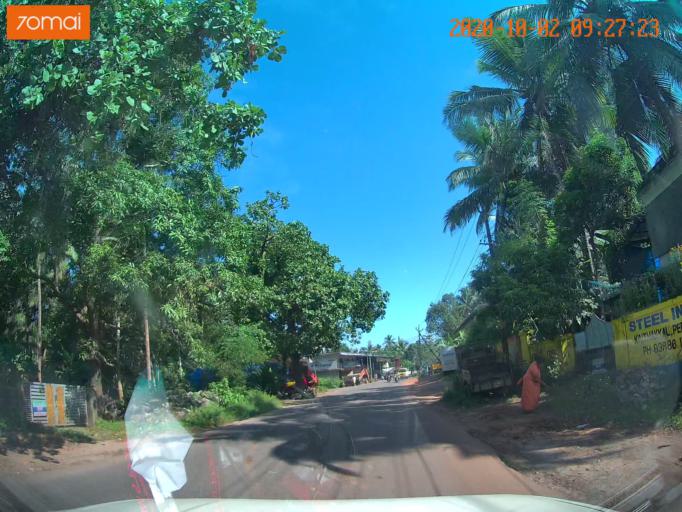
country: IN
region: Kerala
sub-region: Kozhikode
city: Naduvannur
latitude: 11.5981
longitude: 75.7649
